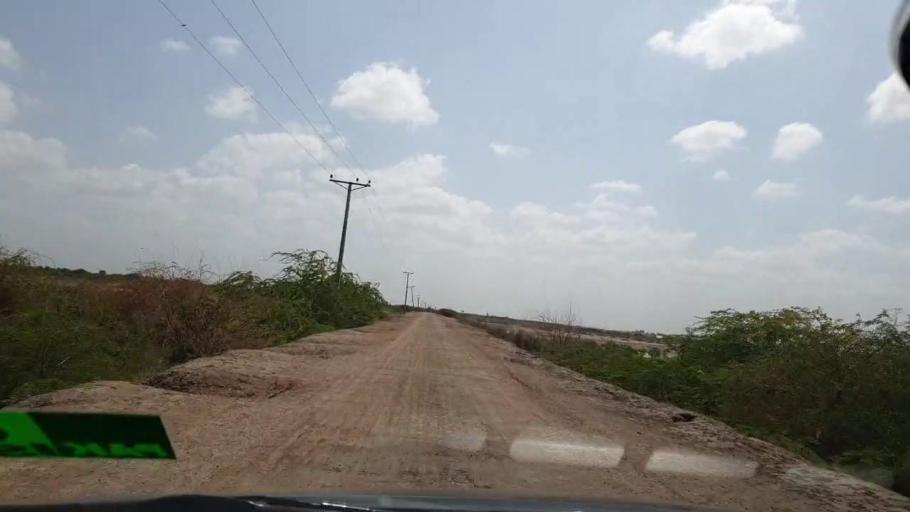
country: PK
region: Sindh
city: Kadhan
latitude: 24.6065
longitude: 69.1852
